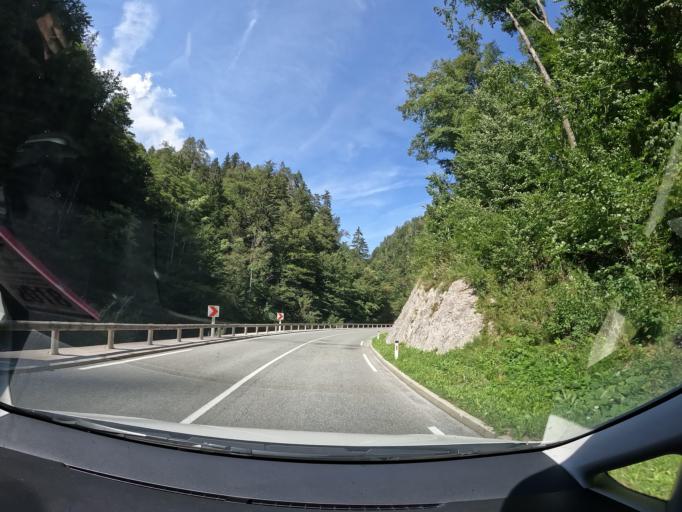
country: SI
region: Trzic
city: Trzic
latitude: 46.4031
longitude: 14.3239
